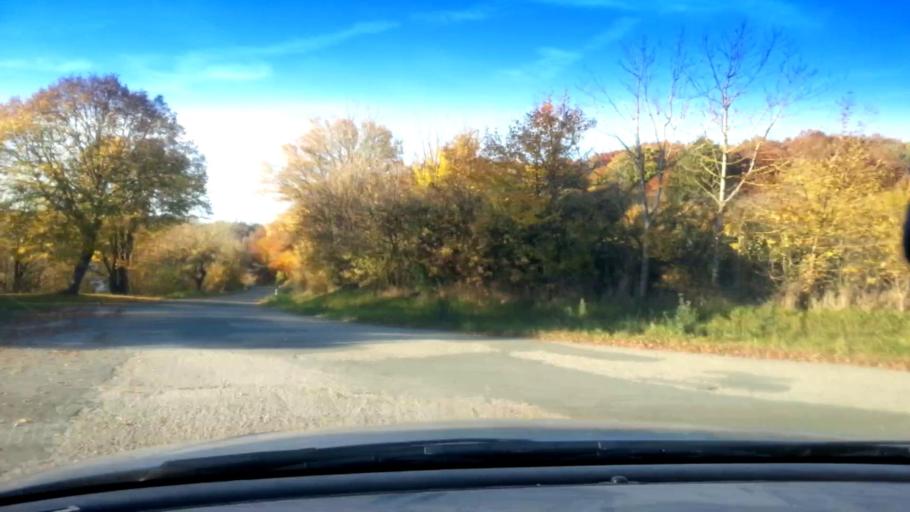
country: DE
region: Bavaria
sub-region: Upper Franconia
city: Heiligenstadt
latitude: 49.8650
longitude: 11.1808
